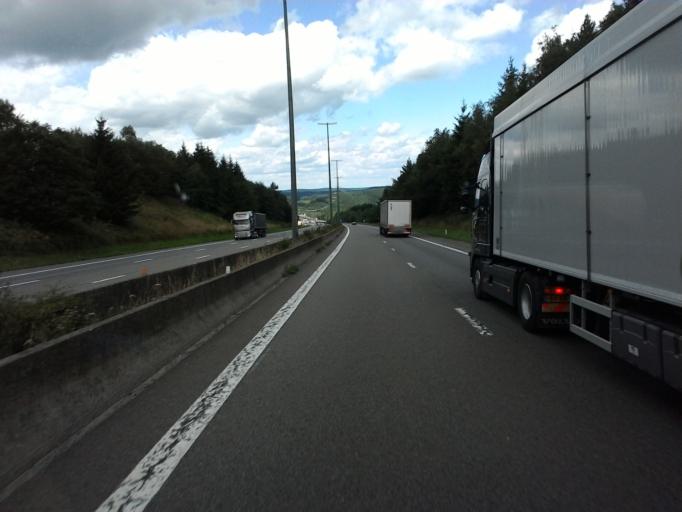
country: BE
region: Wallonia
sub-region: Province du Luxembourg
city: Manhay
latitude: 50.2842
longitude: 5.7280
